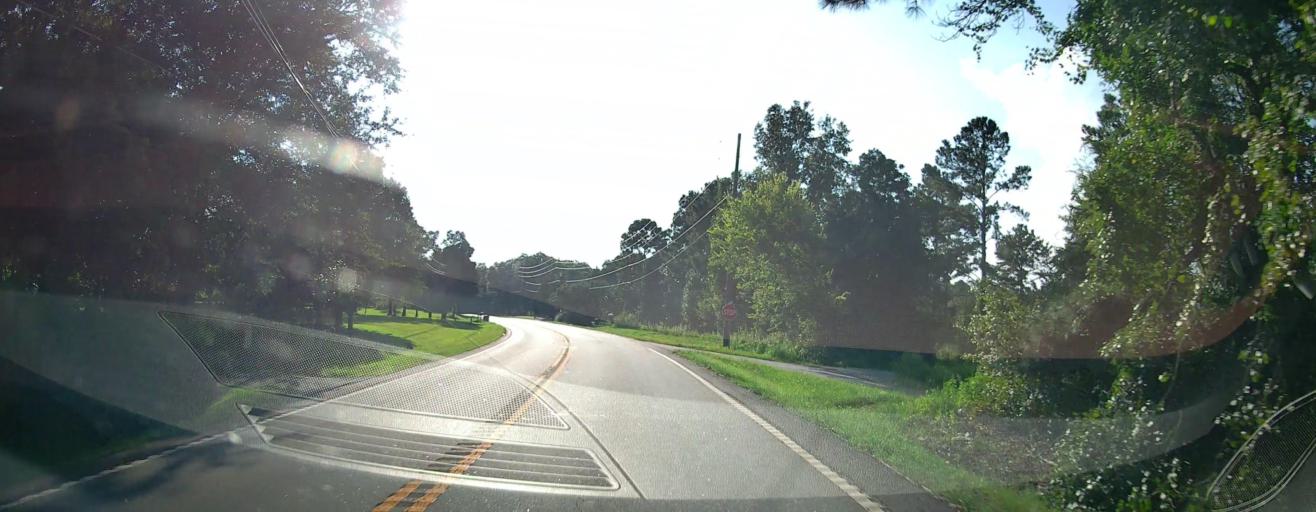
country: US
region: Georgia
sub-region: Houston County
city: Robins Air Force Base
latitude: 32.5026
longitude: -83.6255
